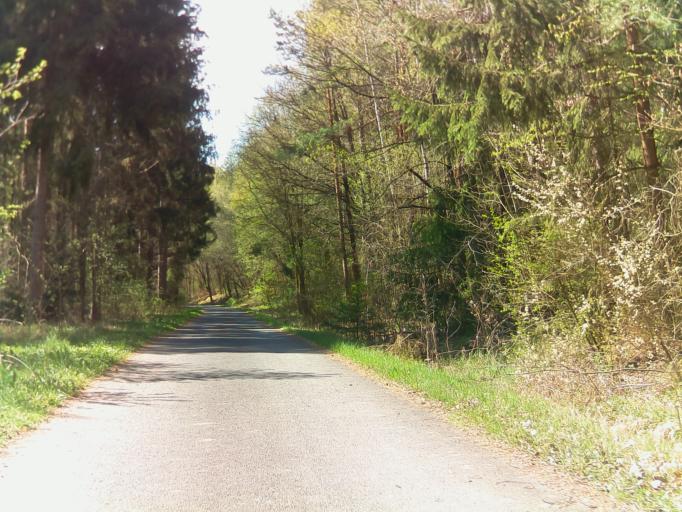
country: DE
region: Thuringia
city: Hellingen
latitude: 50.2868
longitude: 10.7788
